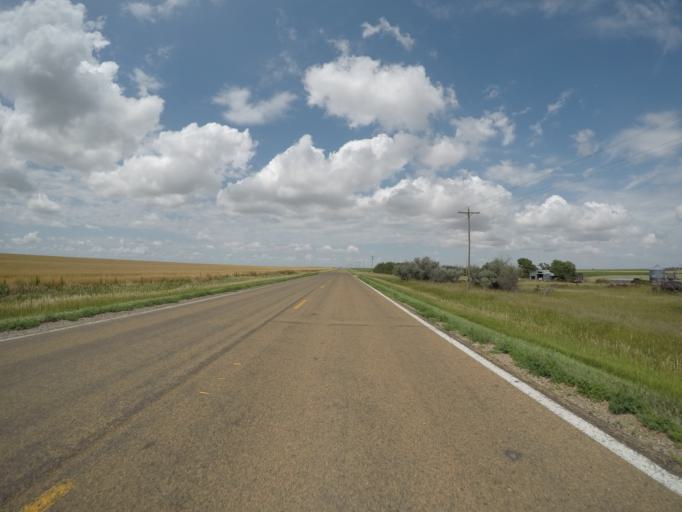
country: US
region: Kansas
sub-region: Rawlins County
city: Atwood
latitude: 39.8946
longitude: -101.0467
